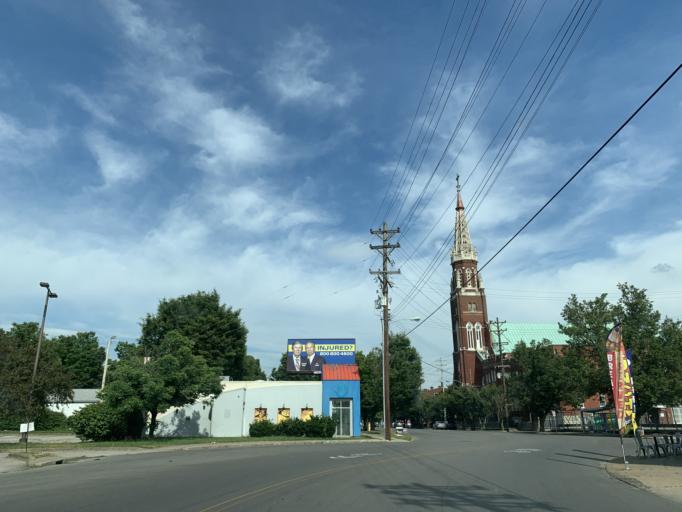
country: US
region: Kentucky
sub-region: Jefferson County
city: Louisville
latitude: 38.2590
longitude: -85.7892
